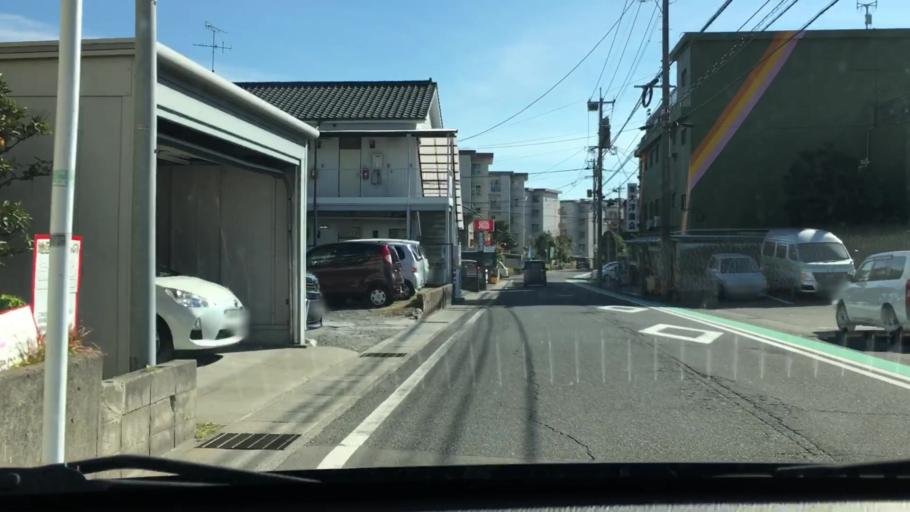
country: JP
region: Kagoshima
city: Kagoshima-shi
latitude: 31.5630
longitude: 130.5315
